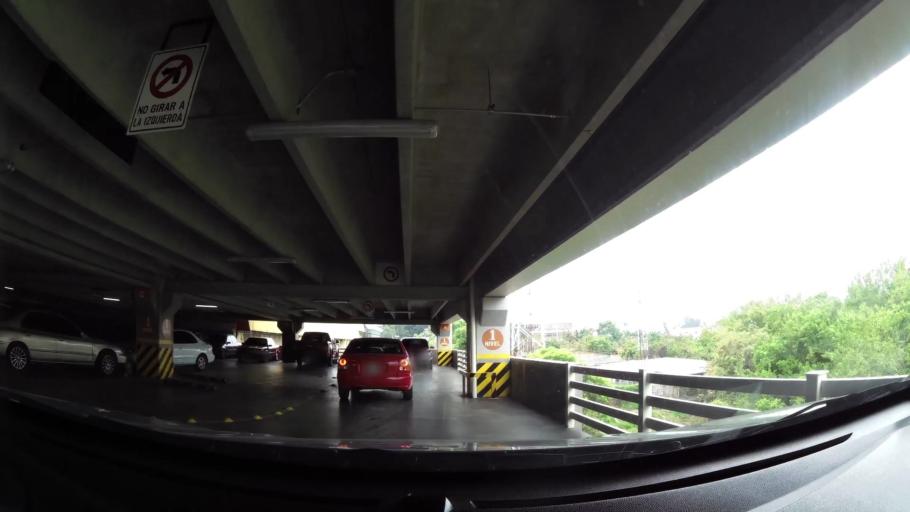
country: HN
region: Francisco Morazan
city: Tegucigalpa
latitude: 14.0778
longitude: -87.1870
